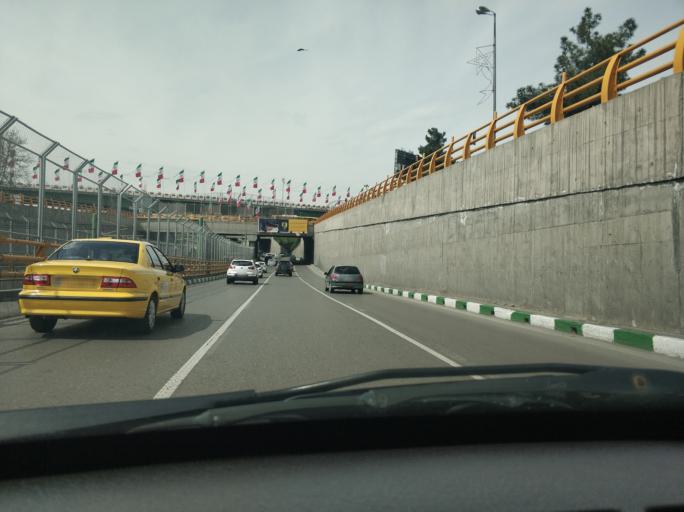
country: IR
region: Razavi Khorasan
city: Mashhad
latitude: 36.3142
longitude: 59.5422
